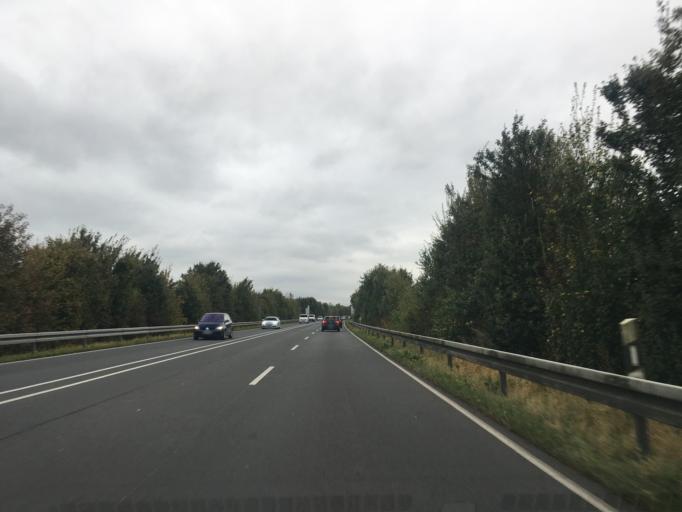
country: DE
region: North Rhine-Westphalia
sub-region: Regierungsbezirk Munster
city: Metelen
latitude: 52.1857
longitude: 7.2340
